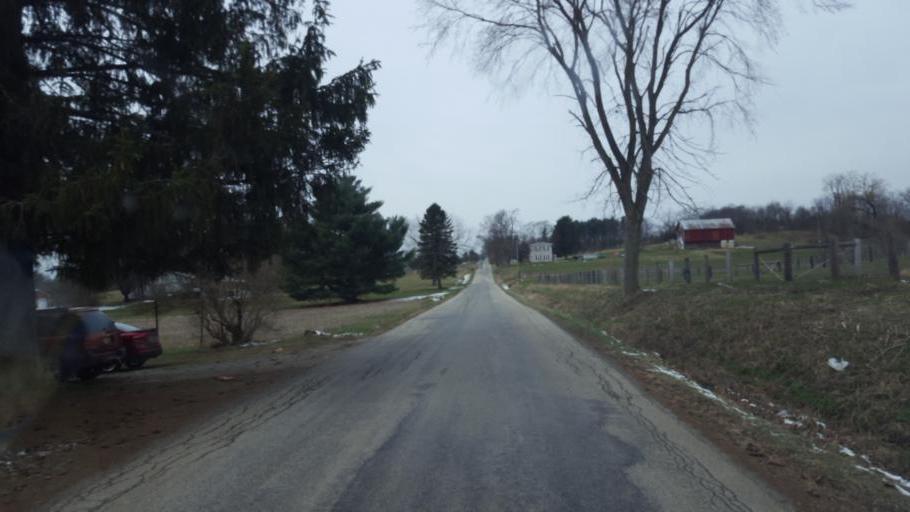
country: US
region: Ohio
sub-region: Sandusky County
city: Bellville
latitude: 40.5946
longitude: -82.5367
